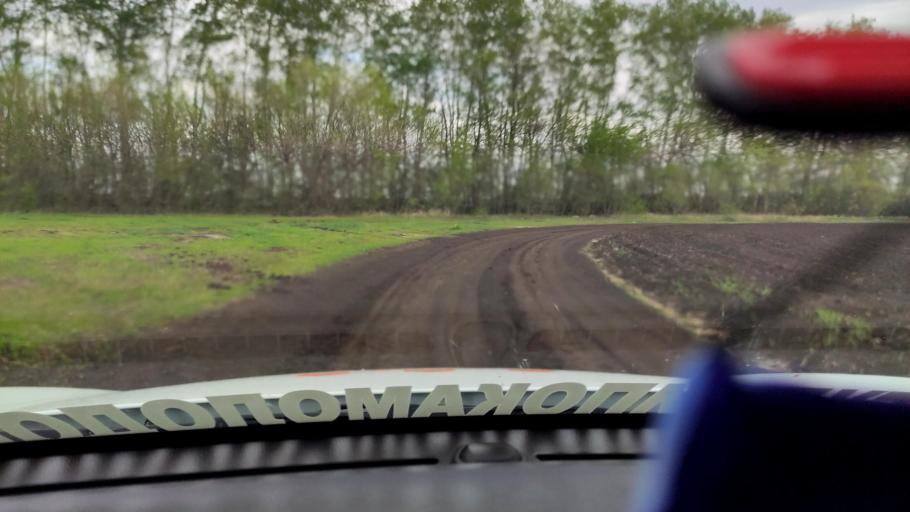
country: RU
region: Voronezj
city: Uryv-Pokrovka
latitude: 51.1501
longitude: 39.1162
